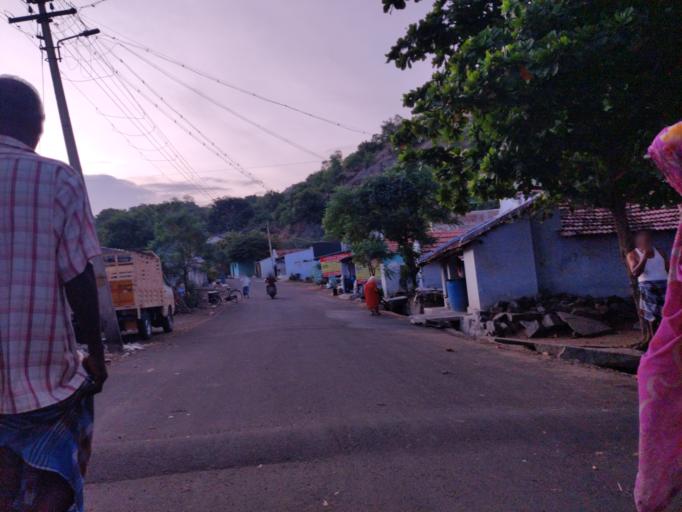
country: IN
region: Tamil Nadu
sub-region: Salem
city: Salem
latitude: 11.6216
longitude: 78.1478
